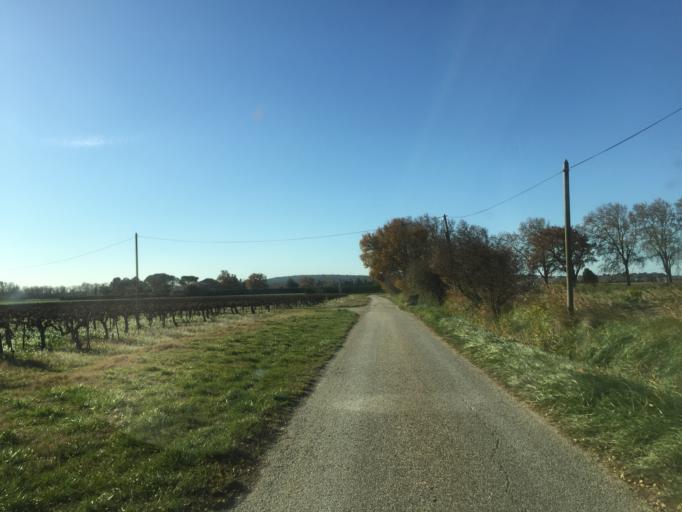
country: FR
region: Provence-Alpes-Cote d'Azur
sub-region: Departement du Vaucluse
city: Bedarrides
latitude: 44.0468
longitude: 4.9263
